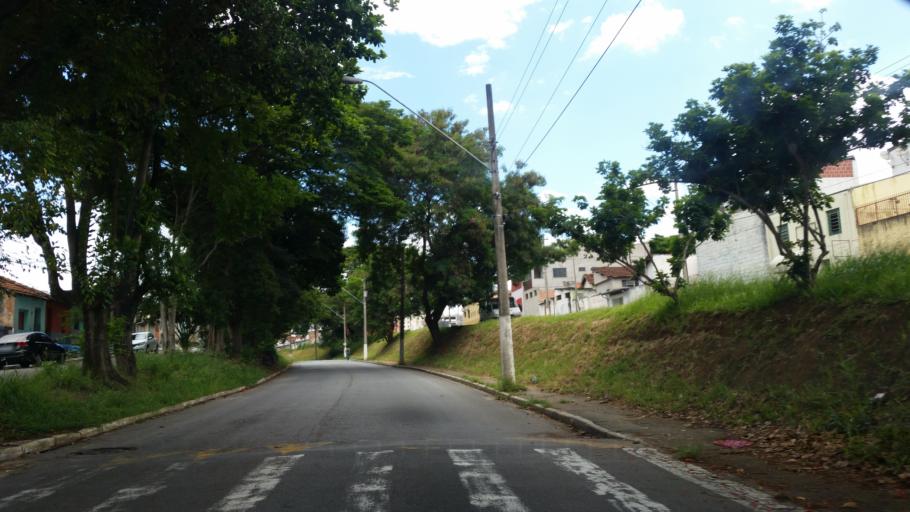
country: BR
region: Sao Paulo
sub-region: Taubate
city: Taubate
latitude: -23.0231
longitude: -45.5688
